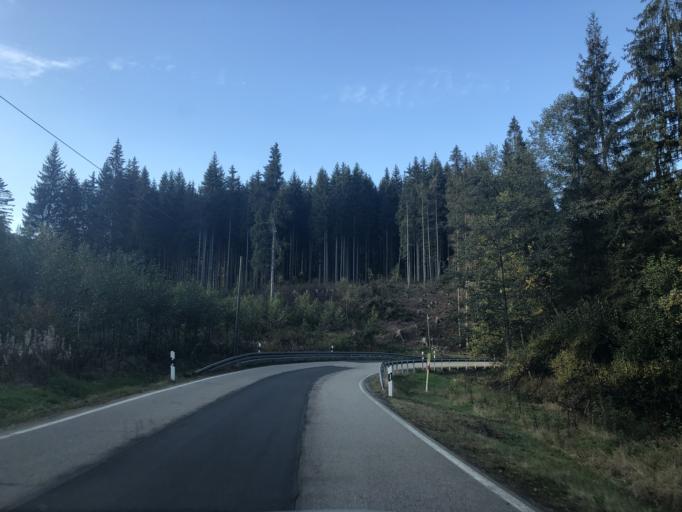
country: DE
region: Bavaria
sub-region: Lower Bavaria
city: Frauenau
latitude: 48.9767
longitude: 13.2988
